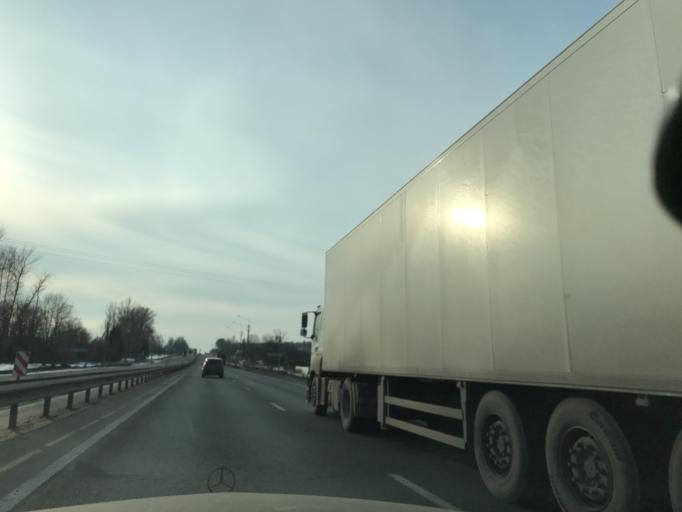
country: RU
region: Vladimir
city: Novki
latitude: 56.2022
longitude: 41.1123
